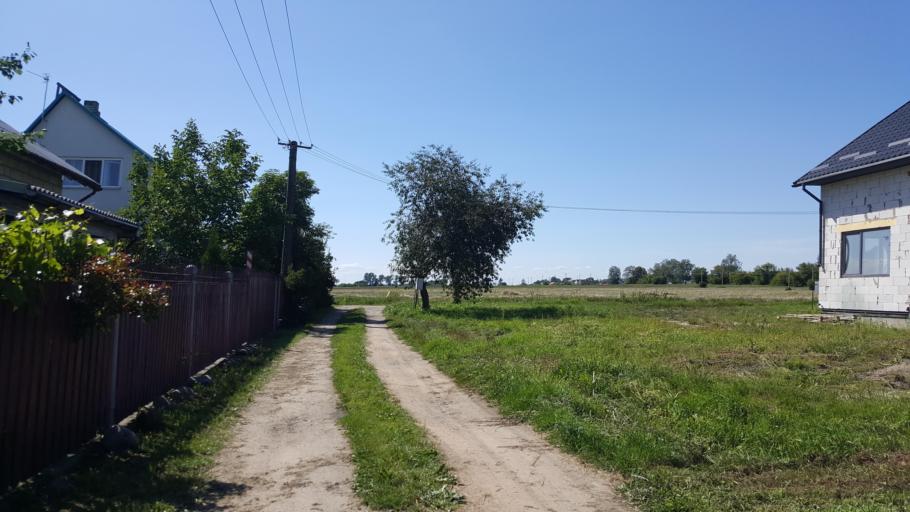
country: BY
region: Brest
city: Charnawchytsy
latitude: 52.2027
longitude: 23.7519
